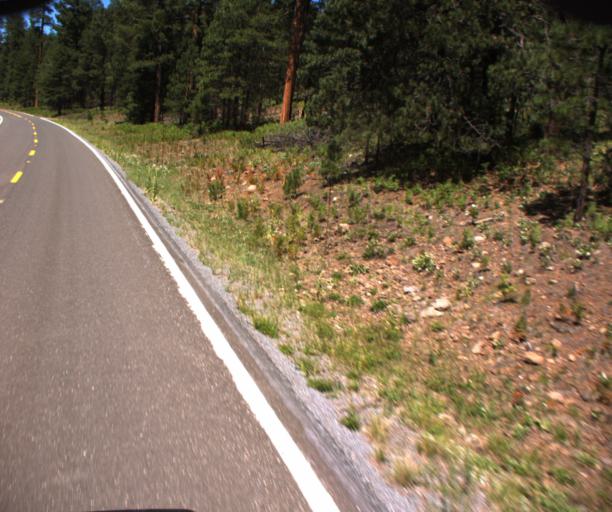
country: US
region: Arizona
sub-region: Apache County
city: Eagar
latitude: 33.6483
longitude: -109.3089
